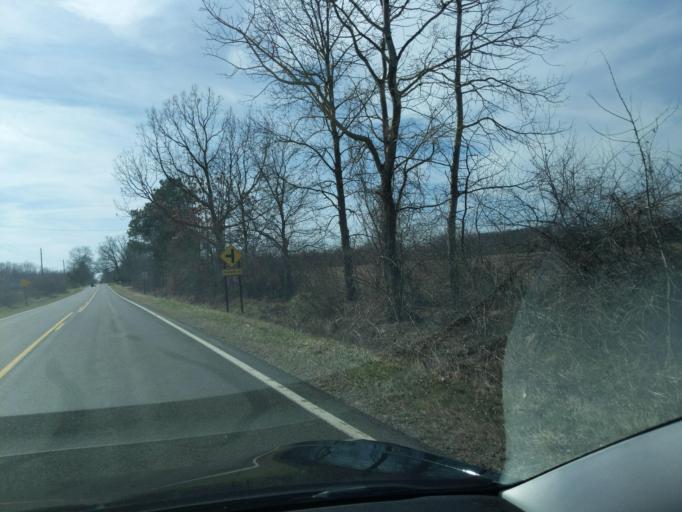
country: US
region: Michigan
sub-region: Ingham County
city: Stockbridge
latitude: 42.4832
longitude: -84.2304
